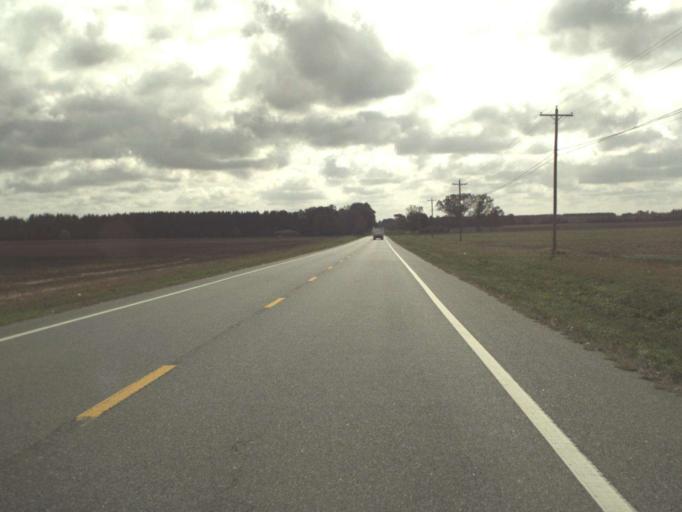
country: US
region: Florida
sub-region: Santa Rosa County
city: Point Baker
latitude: 30.8691
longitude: -87.0526
